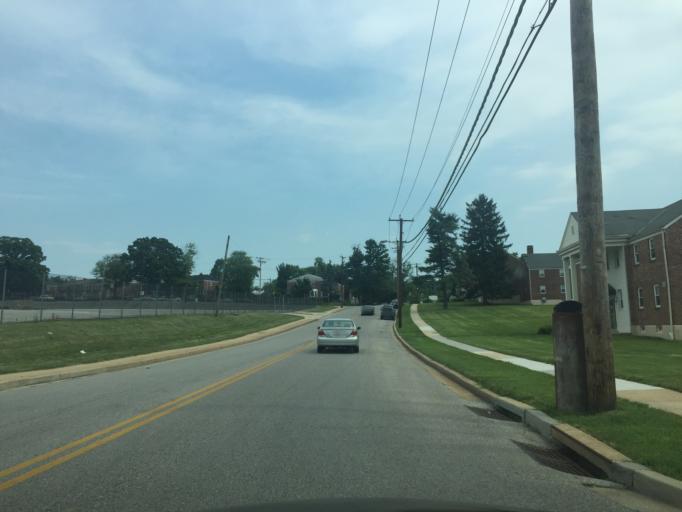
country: US
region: Maryland
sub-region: Baltimore County
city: Parkville
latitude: 39.3588
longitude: -76.5819
